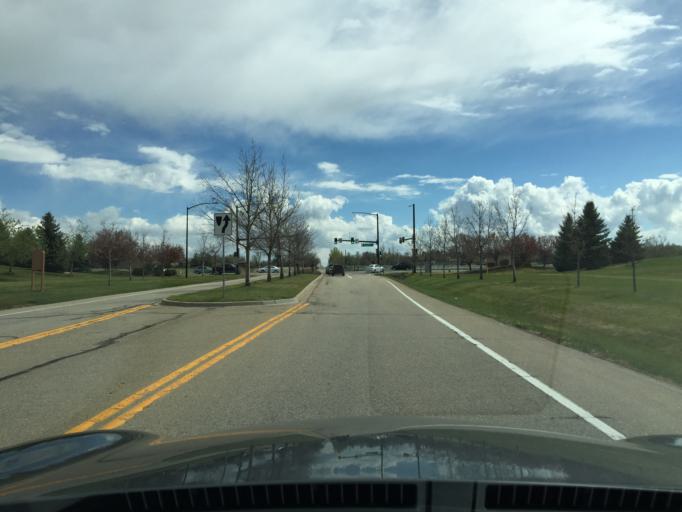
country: US
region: Colorado
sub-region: Boulder County
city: Lafayette
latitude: 40.0157
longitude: -105.0933
